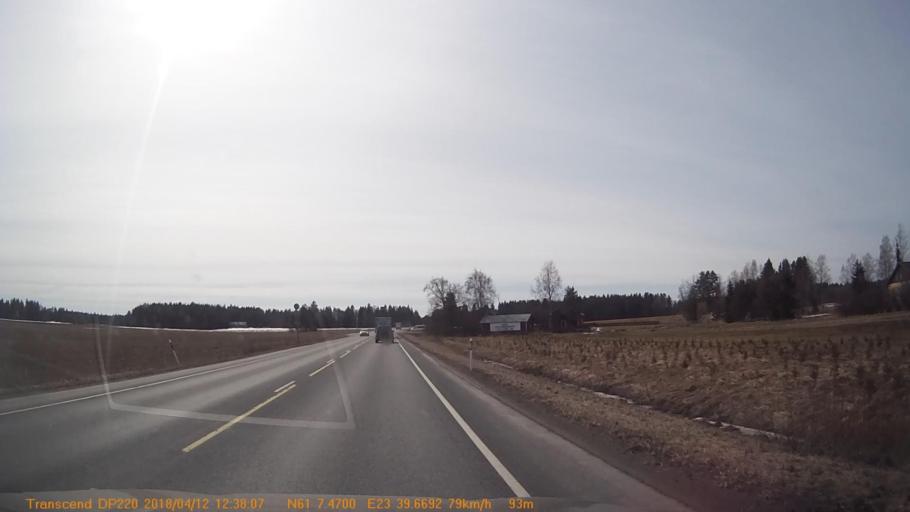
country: FI
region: Pirkanmaa
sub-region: Etelae-Pirkanmaa
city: Kylmaekoski
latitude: 61.1247
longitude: 23.6608
